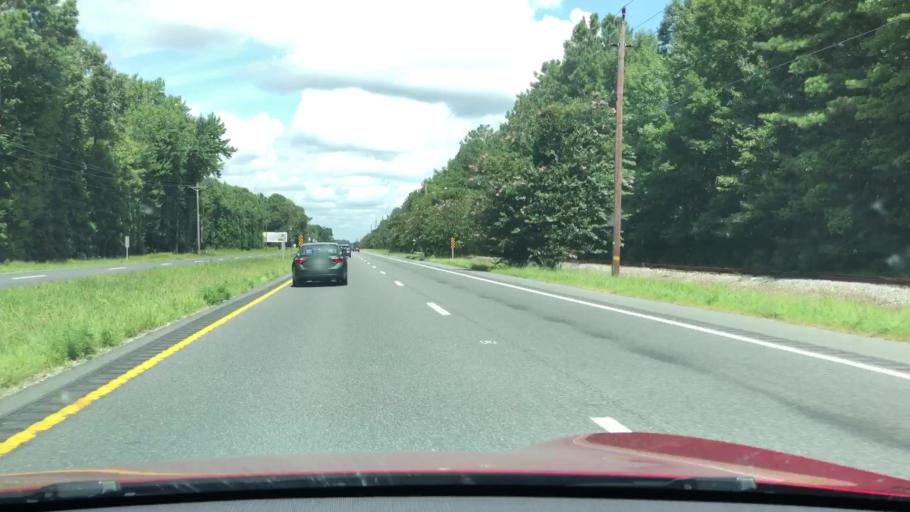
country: US
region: Virginia
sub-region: Northampton County
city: Exmore
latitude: 37.4995
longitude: -75.8423
